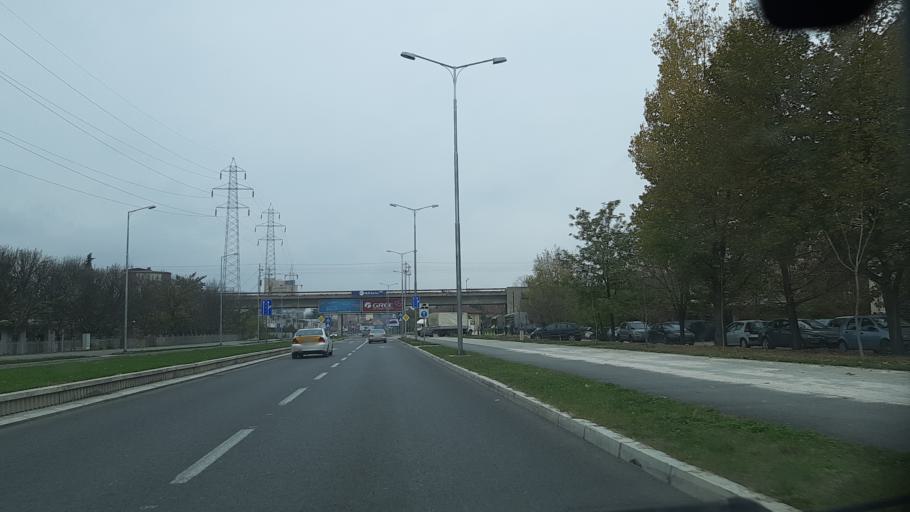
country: MK
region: Karpos
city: Skopje
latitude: 41.9868
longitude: 21.4442
